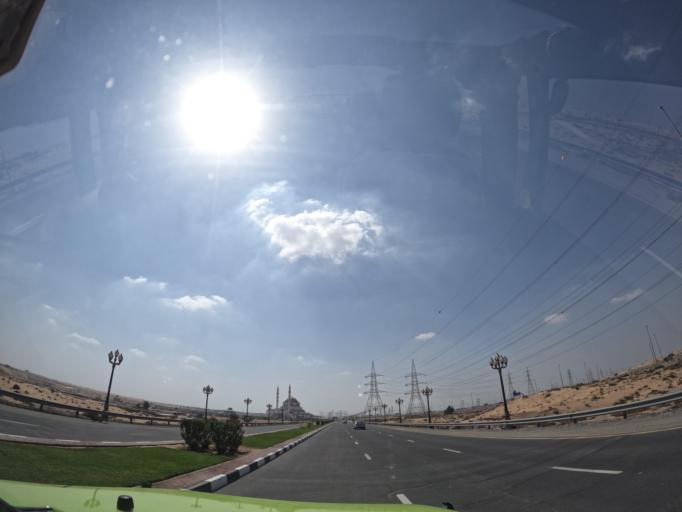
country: AE
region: Ash Shariqah
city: Sharjah
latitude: 25.2469
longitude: 55.5721
